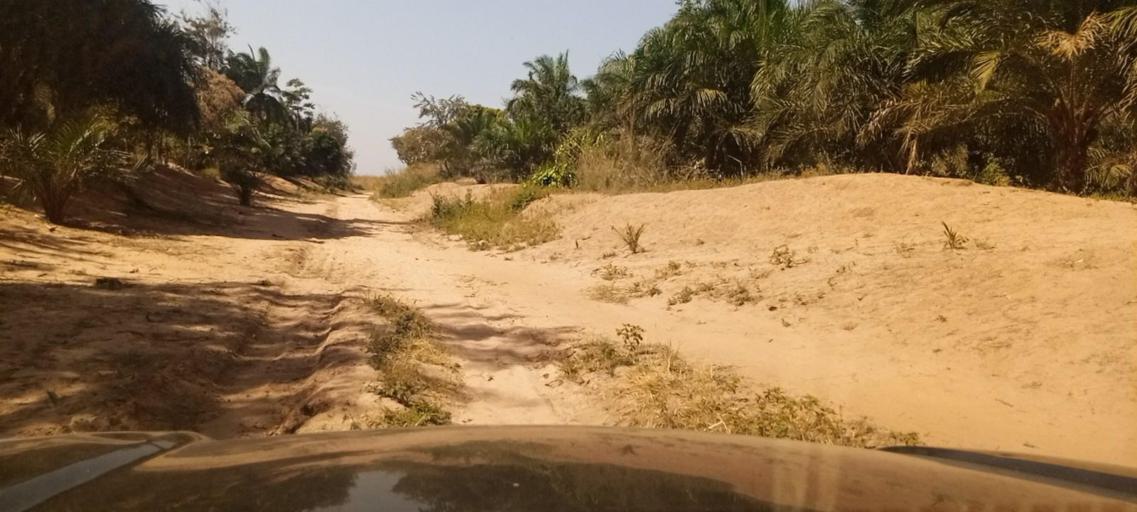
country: CD
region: Kasai-Oriental
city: Kabinda
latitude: -5.8038
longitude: 25.0267
